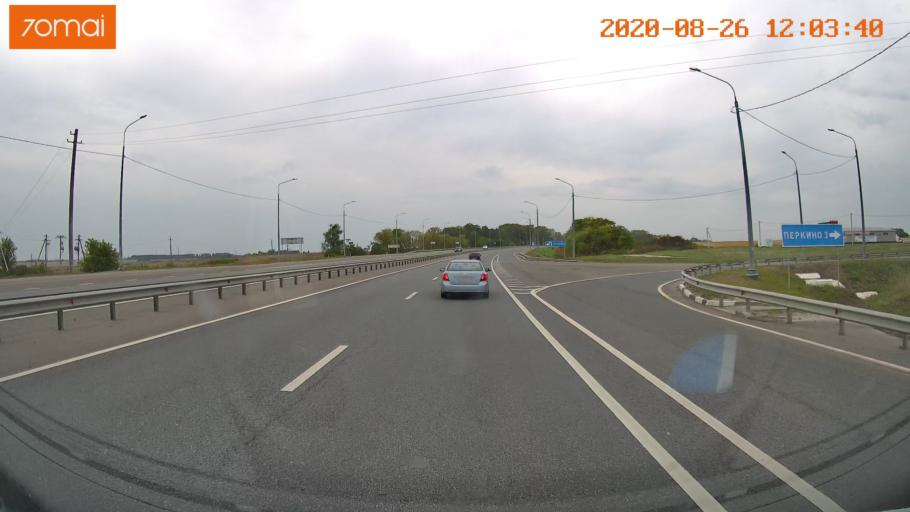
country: RU
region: Rjazan
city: Kiritsy
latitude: 54.3023
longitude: 40.2019
